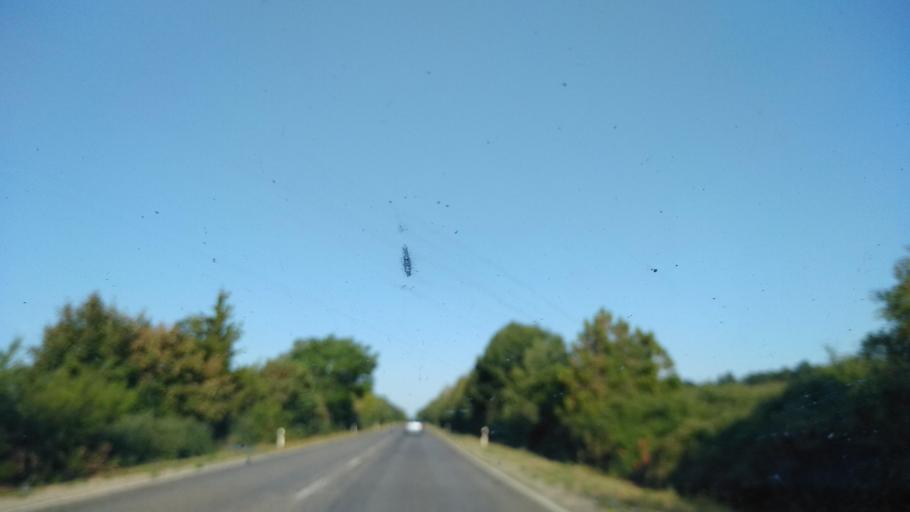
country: BG
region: Gabrovo
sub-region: Obshtina Dryanovo
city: Dryanovo
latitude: 43.0876
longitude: 25.4533
